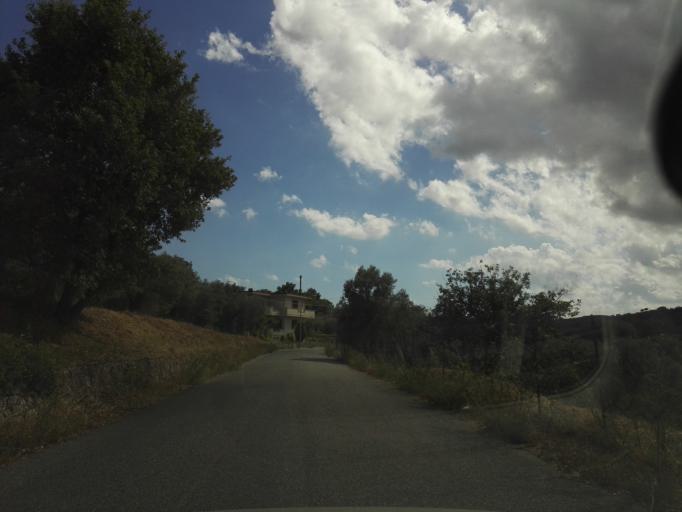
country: IT
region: Calabria
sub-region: Provincia di Reggio Calabria
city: Camini
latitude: 38.4298
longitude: 16.4952
